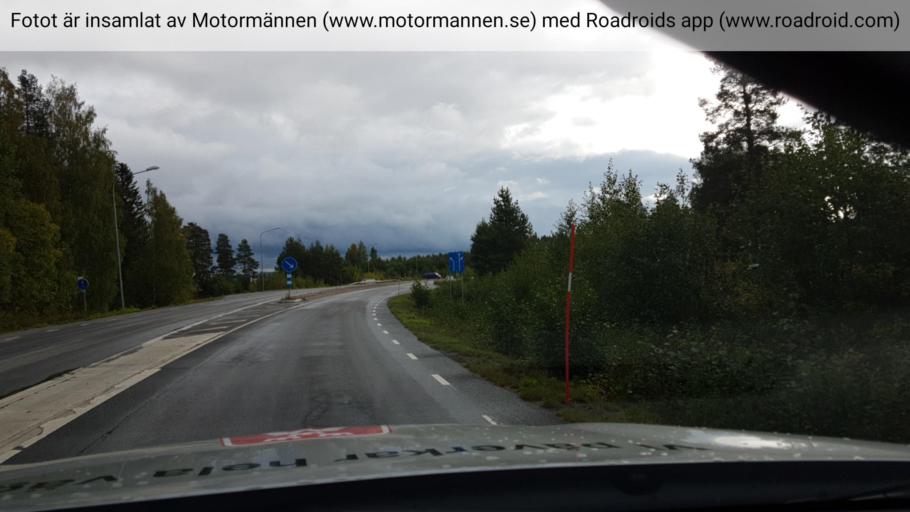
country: SE
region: Norrbotten
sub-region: Bodens Kommun
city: Boden
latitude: 65.8158
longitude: 21.6452
